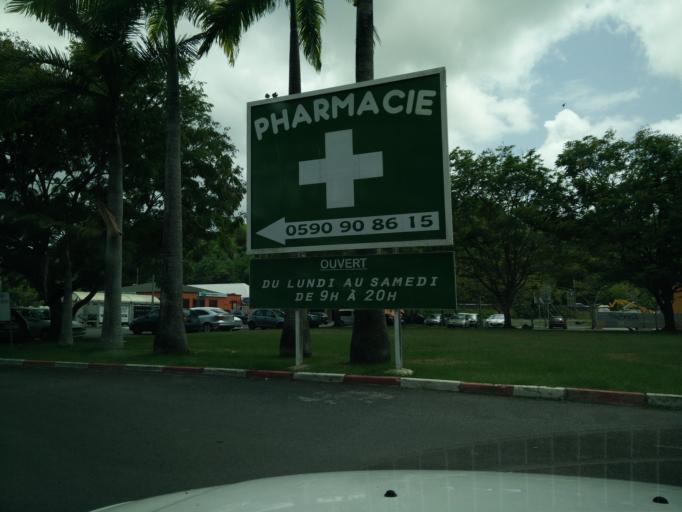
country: GP
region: Guadeloupe
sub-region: Guadeloupe
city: Le Gosier
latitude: 16.2176
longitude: -61.5151
